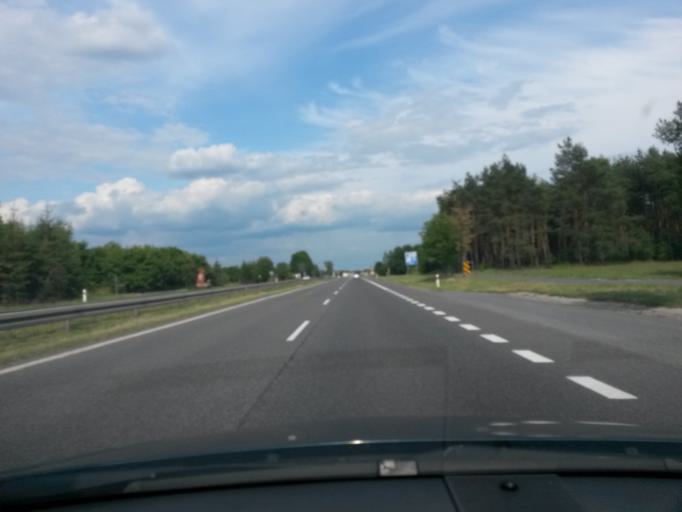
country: PL
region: Masovian Voivodeship
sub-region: Powiat zyrardowski
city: Radziejowice
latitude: 52.0040
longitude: 20.5818
